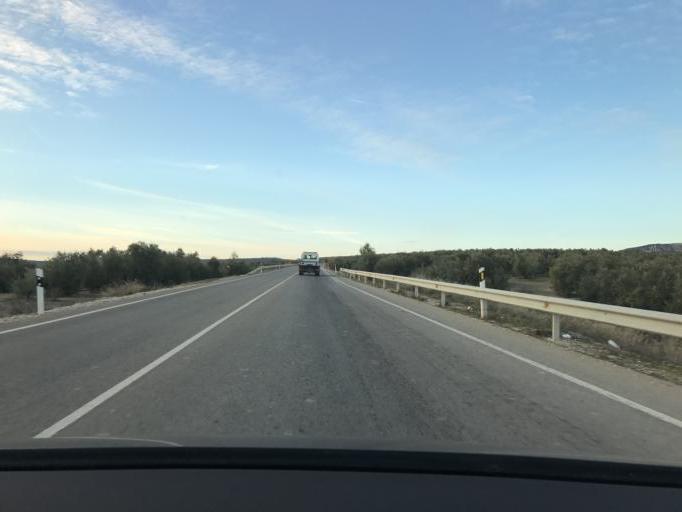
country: ES
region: Andalusia
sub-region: Provincia de Jaen
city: Ubeda
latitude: 37.9744
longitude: -3.3760
